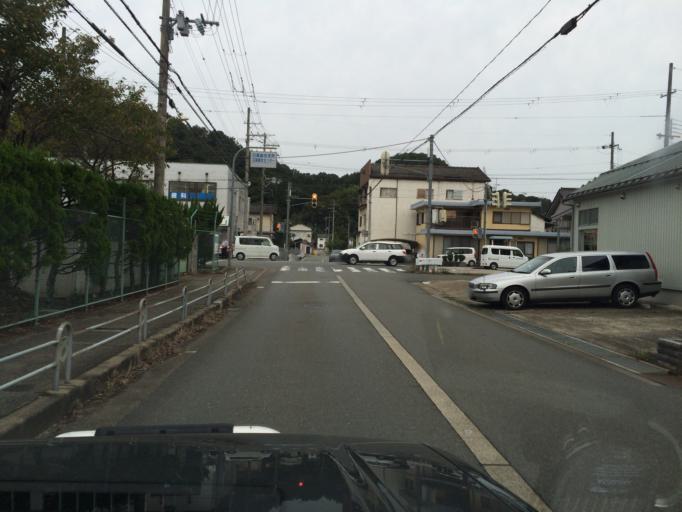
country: JP
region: Hyogo
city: Toyooka
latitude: 35.4697
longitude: 134.7741
